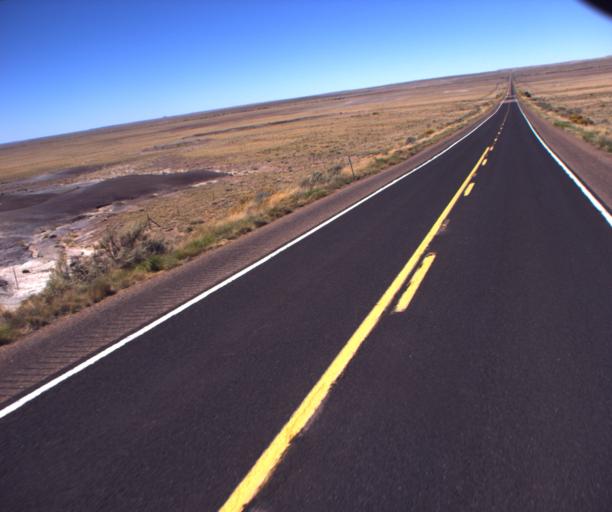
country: US
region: Arizona
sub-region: Navajo County
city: Snowflake
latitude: 34.7178
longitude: -109.7698
